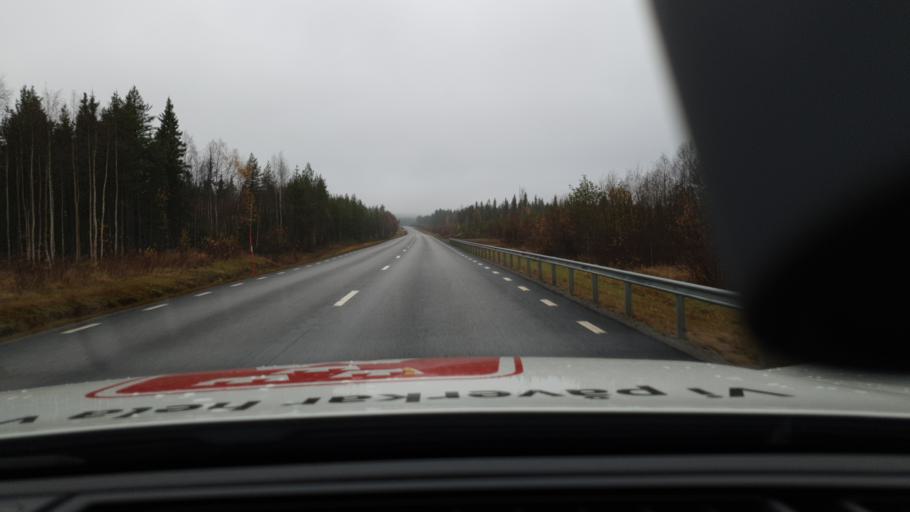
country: SE
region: Norrbotten
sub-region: Overkalix Kommun
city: OEverkalix
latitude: 66.6230
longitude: 22.2259
